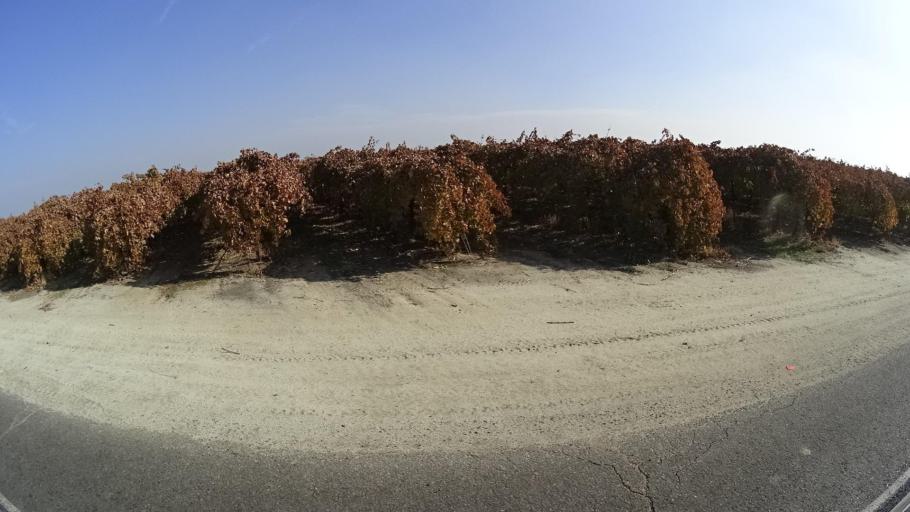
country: US
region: California
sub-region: Kern County
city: McFarland
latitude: 35.6816
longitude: -119.1821
